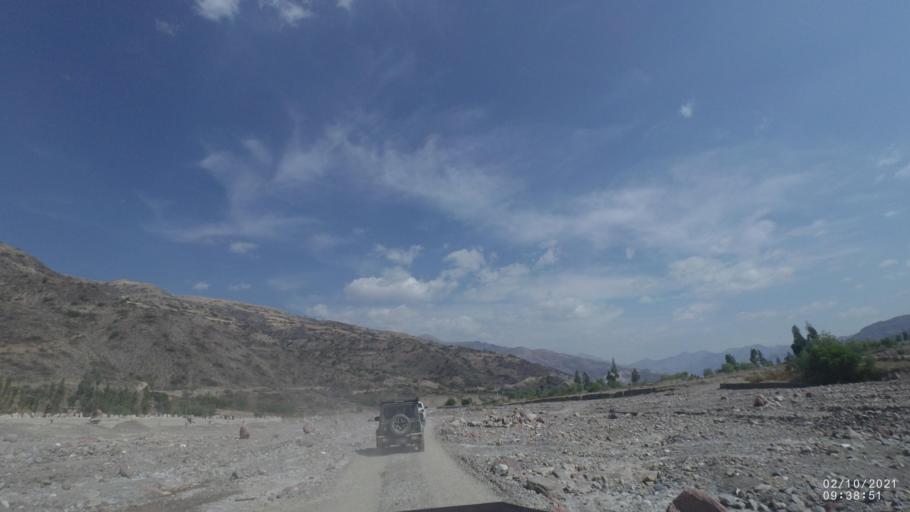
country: BO
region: Cochabamba
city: Irpa Irpa
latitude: -17.8267
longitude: -66.3261
